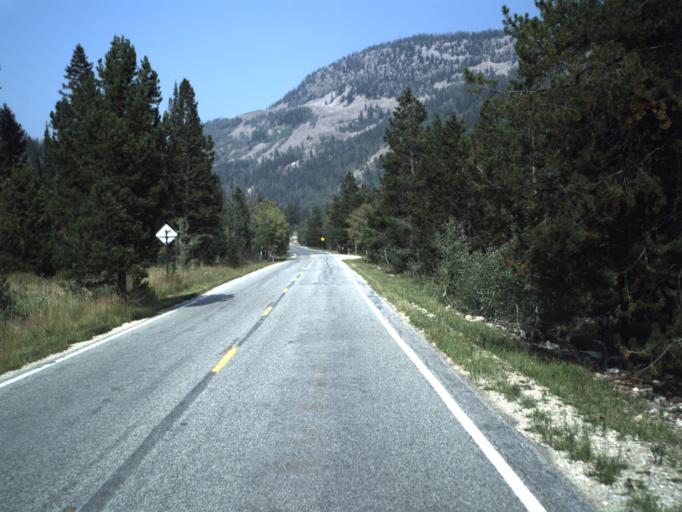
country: US
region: Utah
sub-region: Summit County
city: Francis
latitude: 40.5989
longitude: -110.9711
